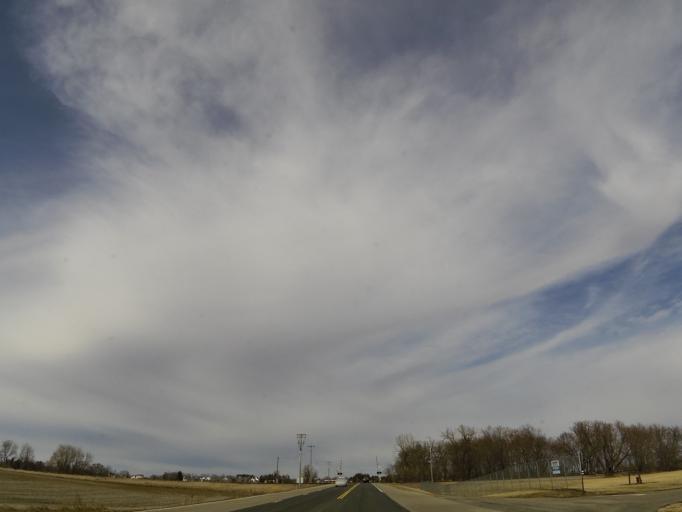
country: US
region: Minnesota
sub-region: Washington County
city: Lake Elmo
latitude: 45.0008
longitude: -92.8628
